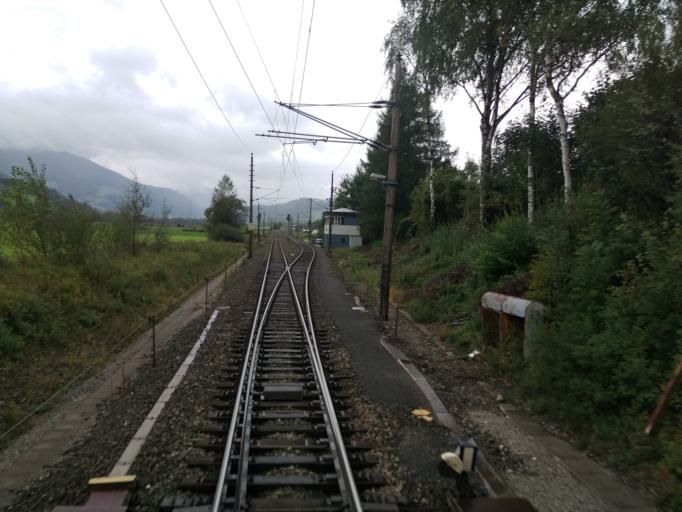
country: AT
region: Styria
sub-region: Politischer Bezirk Liezen
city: Niederoblarn
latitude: 47.4990
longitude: 14.0348
